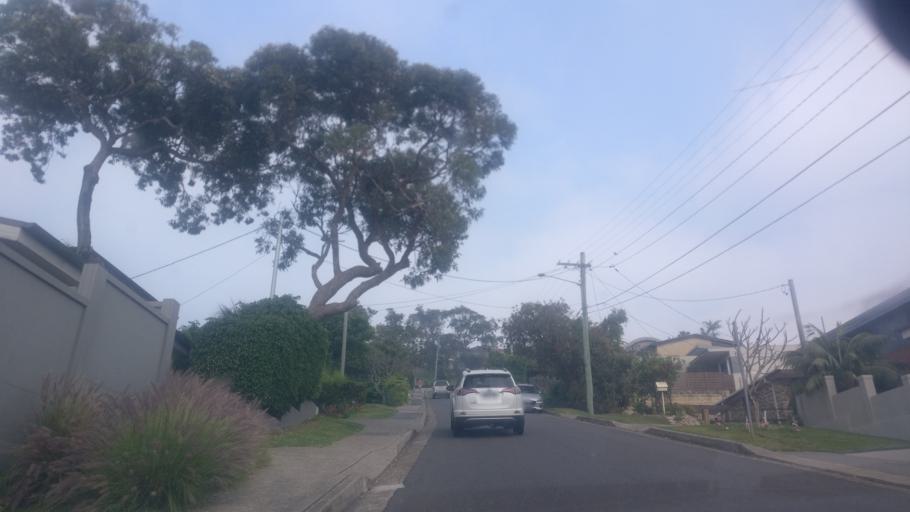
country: AU
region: New South Wales
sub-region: Warringah
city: Dee Why
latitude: -33.7323
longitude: 151.2976
